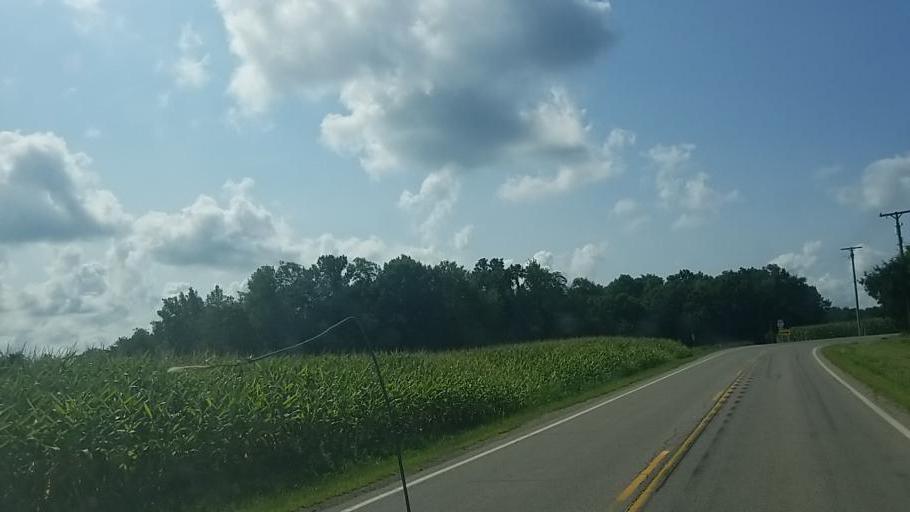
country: US
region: Ohio
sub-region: Ashland County
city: Ashland
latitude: 40.7560
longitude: -82.3071
